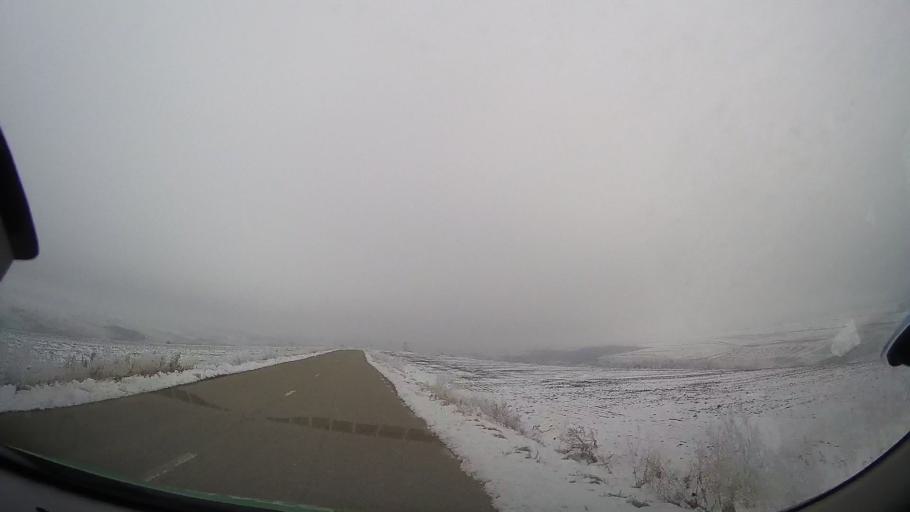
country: RO
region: Vaslui
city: Coroiesti
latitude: 46.2145
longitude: 27.4809
